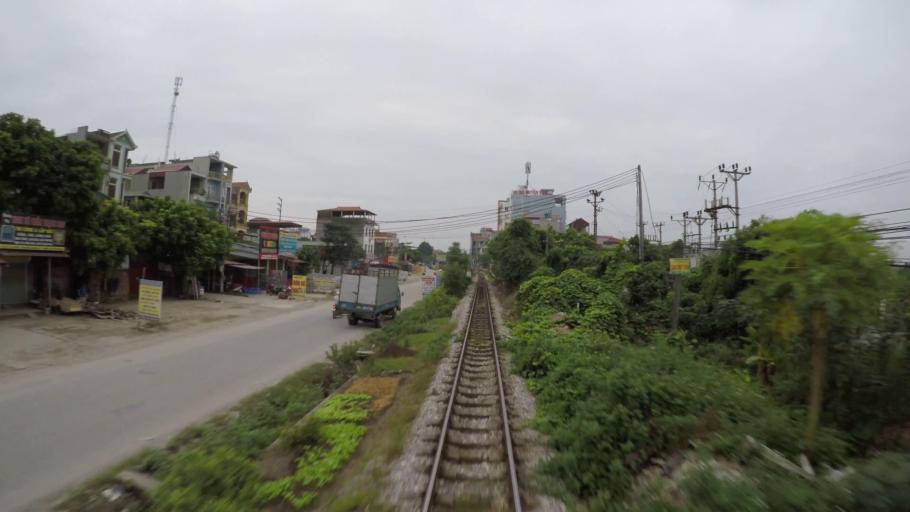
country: VN
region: Hung Yen
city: Nhu Quynh
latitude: 20.9768
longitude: 106.0087
